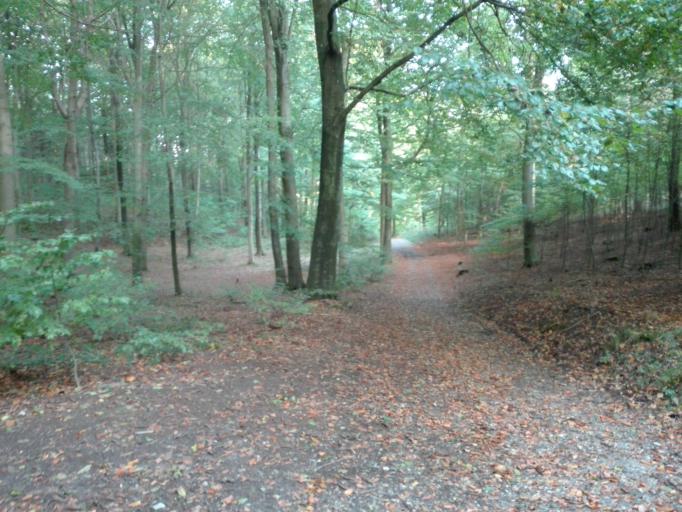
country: DK
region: Central Jutland
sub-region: Arhus Kommune
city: Beder
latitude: 56.0960
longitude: 10.2283
